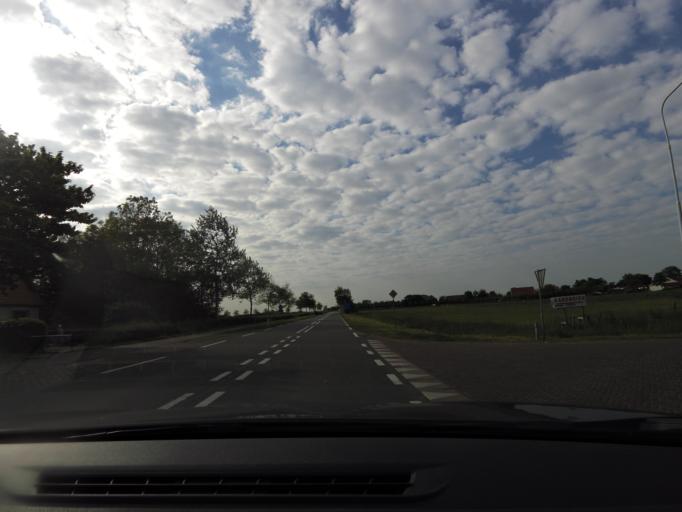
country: NL
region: Zeeland
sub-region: Schouwen-Duiveland
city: Renesse
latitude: 51.7211
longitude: 3.7948
